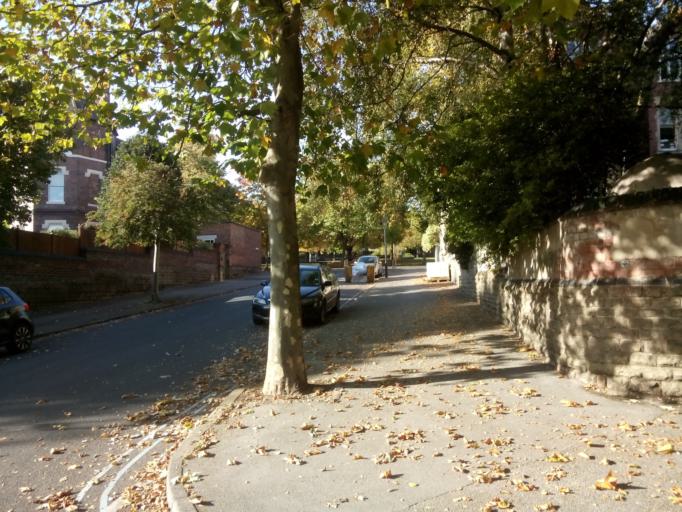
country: GB
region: England
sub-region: Nottingham
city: Nottingham
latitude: 52.9498
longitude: -1.1632
